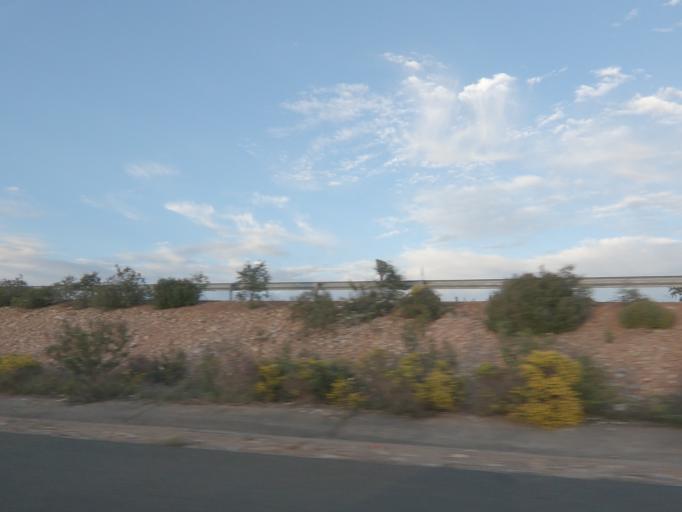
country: ES
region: Extremadura
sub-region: Provincia de Caceres
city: Alcuescar
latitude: 39.1438
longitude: -6.2740
